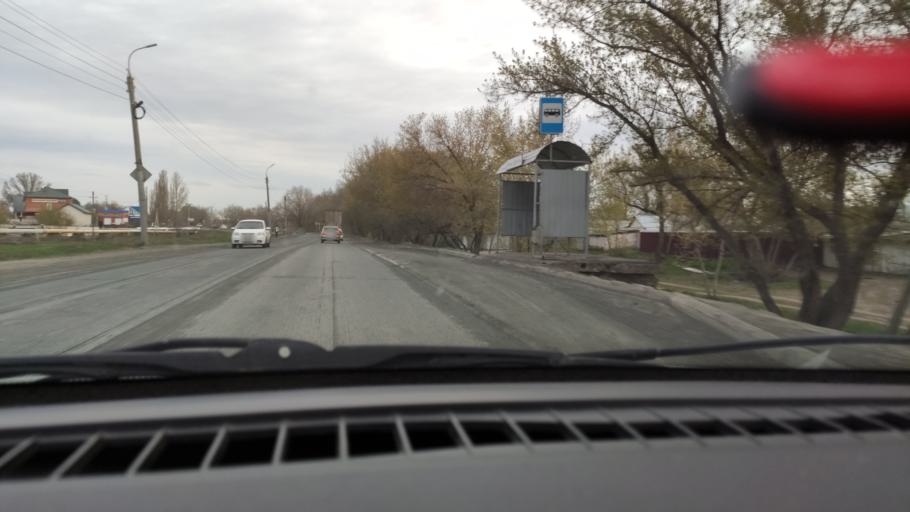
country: RU
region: Orenburg
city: Orenburg
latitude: 51.8605
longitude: 55.1345
